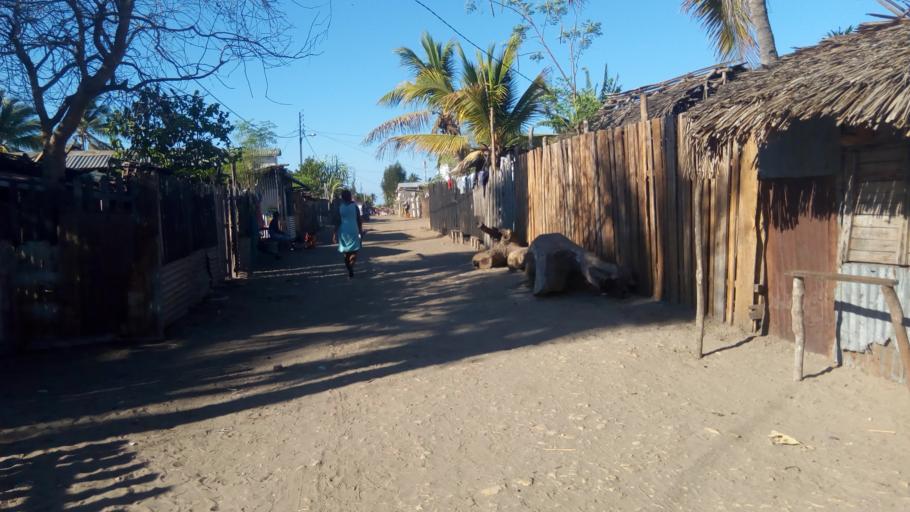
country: MG
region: Menabe
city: Morondava
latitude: -20.2990
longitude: 44.2791
